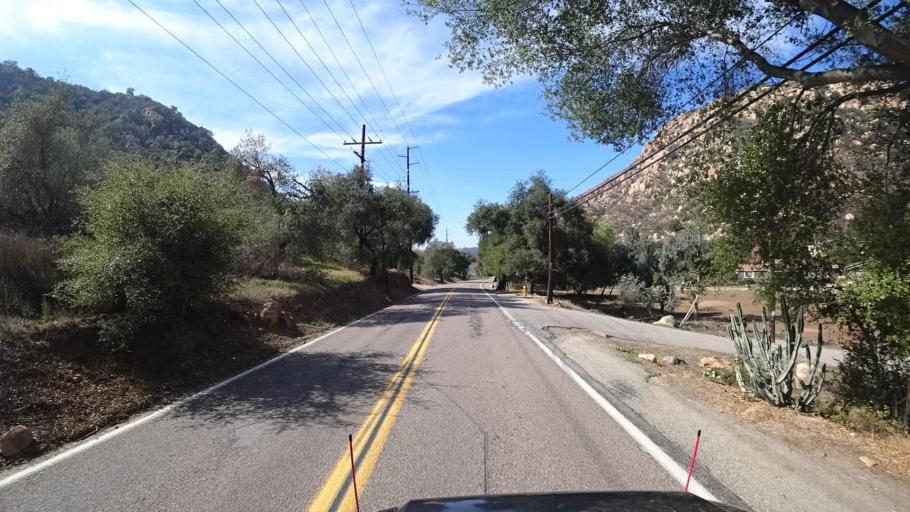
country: US
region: California
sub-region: San Diego County
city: Harbison Canyon
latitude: 32.8285
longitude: -116.8191
